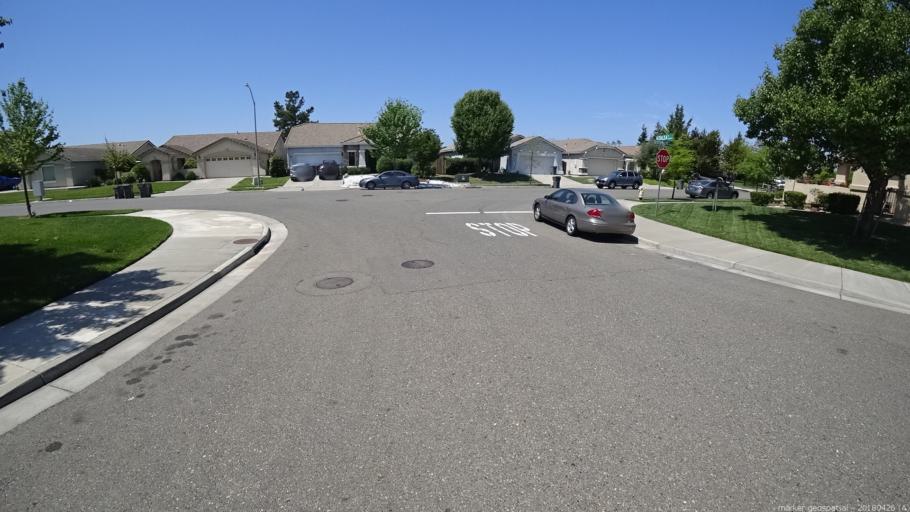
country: US
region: California
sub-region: Yolo County
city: West Sacramento
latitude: 38.5361
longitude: -121.5567
